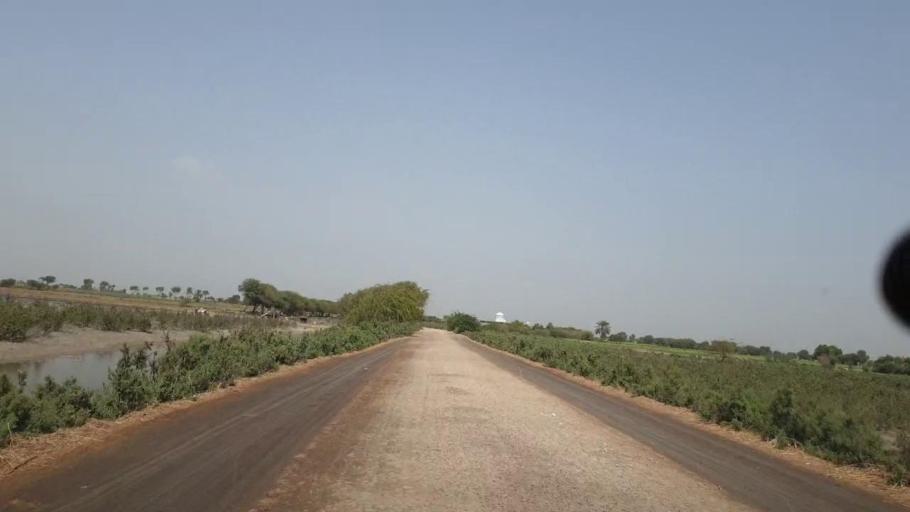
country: PK
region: Sindh
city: Matli
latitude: 25.0684
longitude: 68.7073
